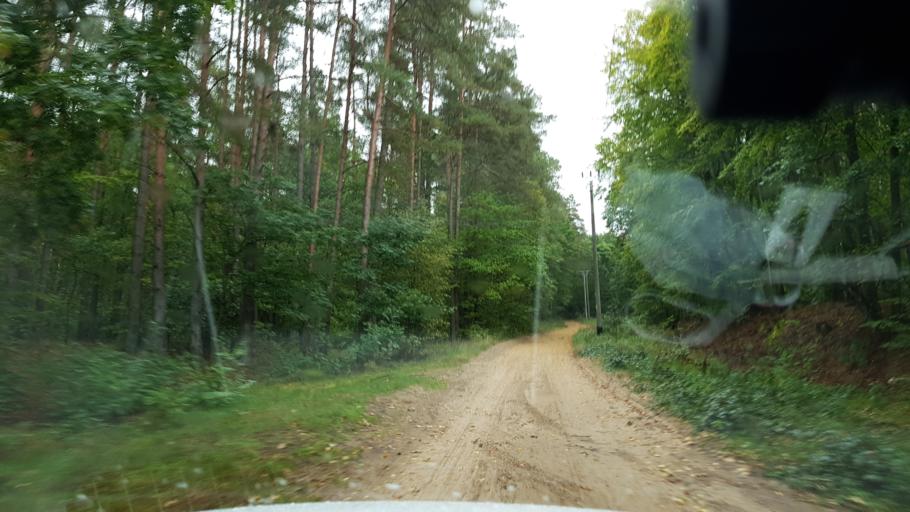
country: PL
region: West Pomeranian Voivodeship
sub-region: Powiat goleniowski
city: Przybiernow
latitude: 53.7487
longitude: 14.7549
